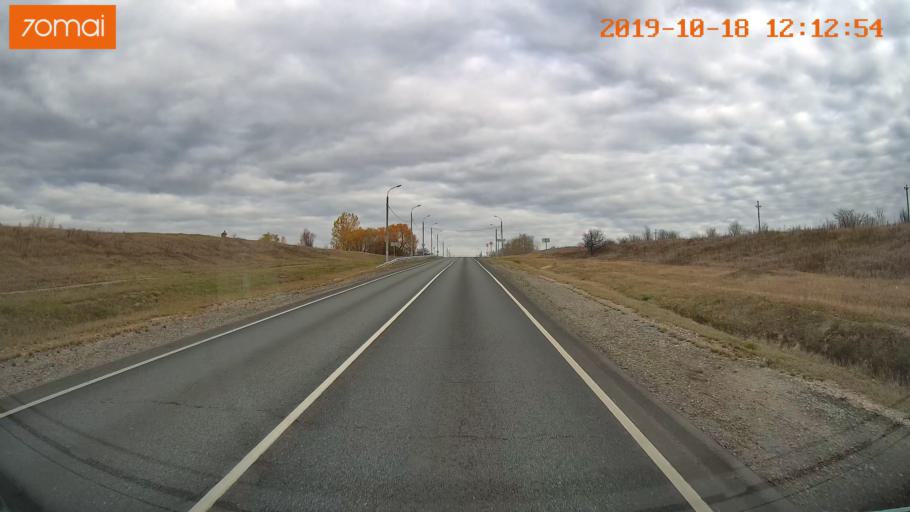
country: RU
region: Rjazan
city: Zakharovo
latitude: 54.4166
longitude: 39.3643
